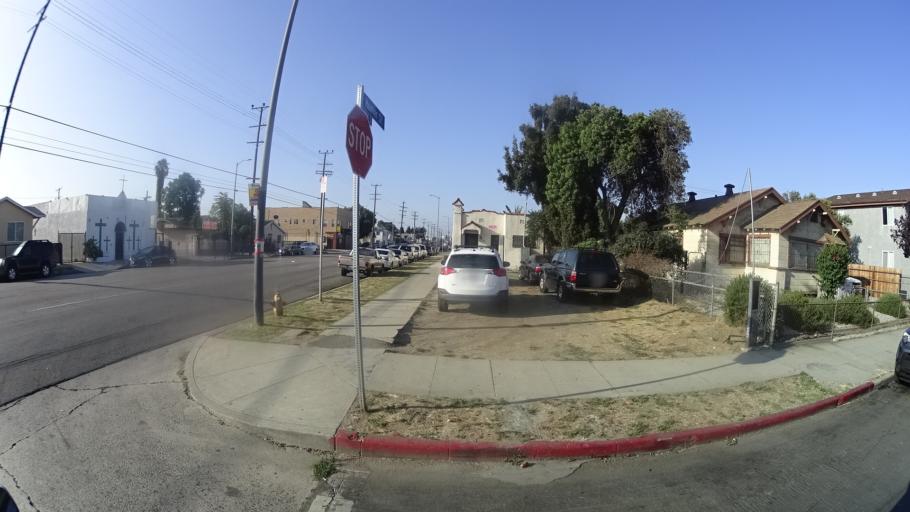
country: US
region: California
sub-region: Los Angeles County
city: Westmont
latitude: 33.9801
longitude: -118.2873
